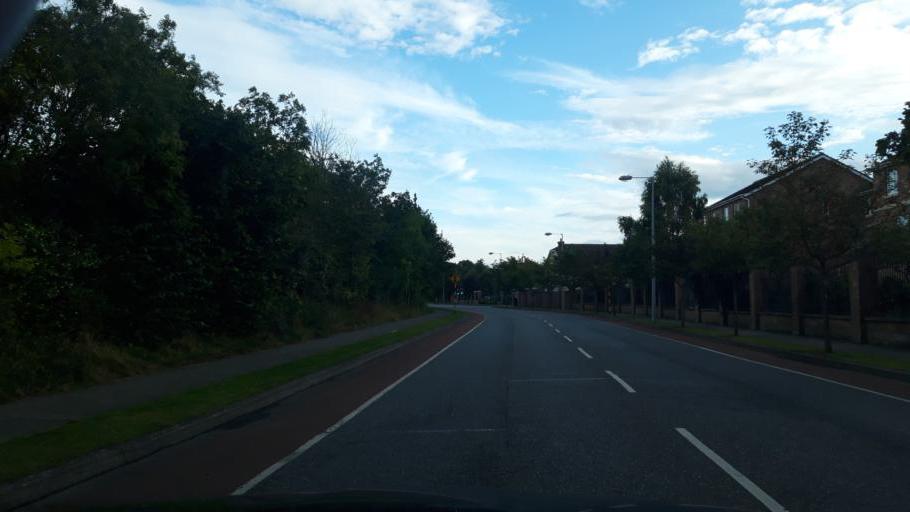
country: IE
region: Leinster
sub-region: Kildare
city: Celbridge
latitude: 53.3374
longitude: -6.5309
